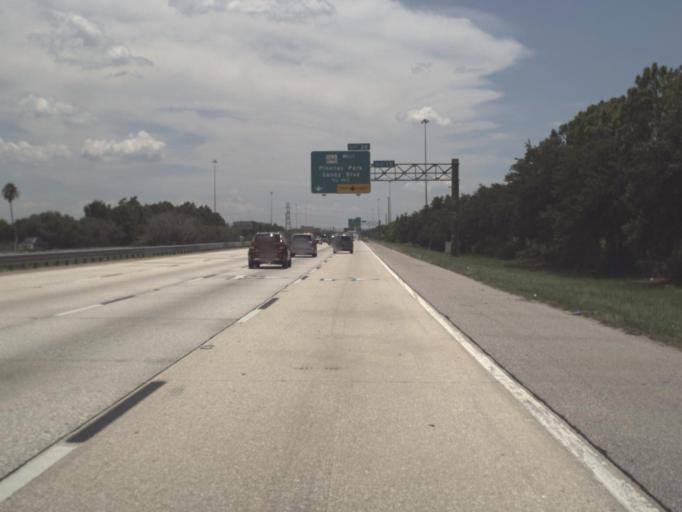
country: US
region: Florida
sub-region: Pinellas County
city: Feather Sound
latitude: 27.8693
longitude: -82.6645
